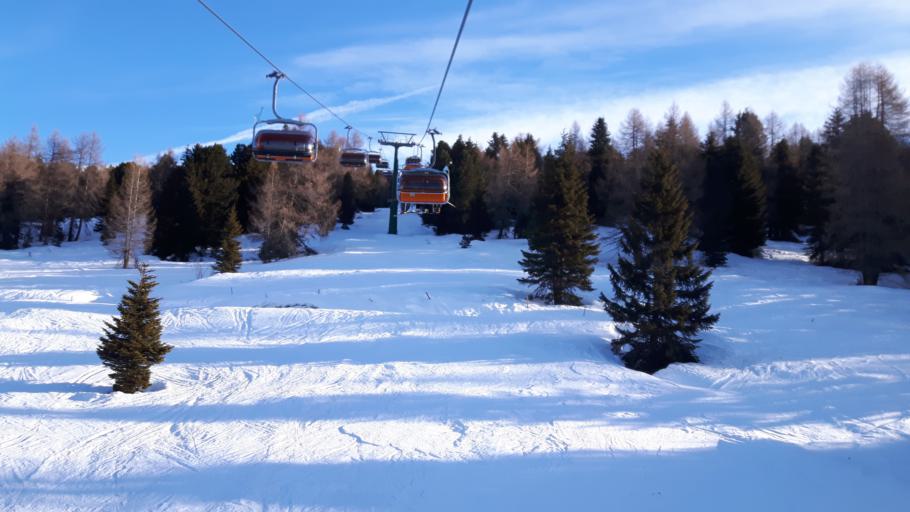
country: IT
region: Trentino-Alto Adige
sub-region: Provincia di Trento
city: Moena
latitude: 46.3357
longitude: 11.7070
